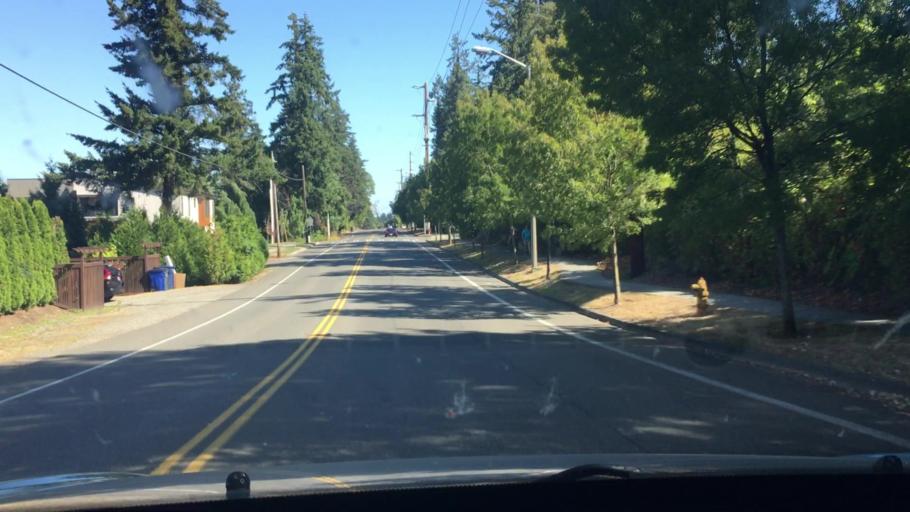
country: US
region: Washington
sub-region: King County
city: Newcastle
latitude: 47.5374
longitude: -122.1856
